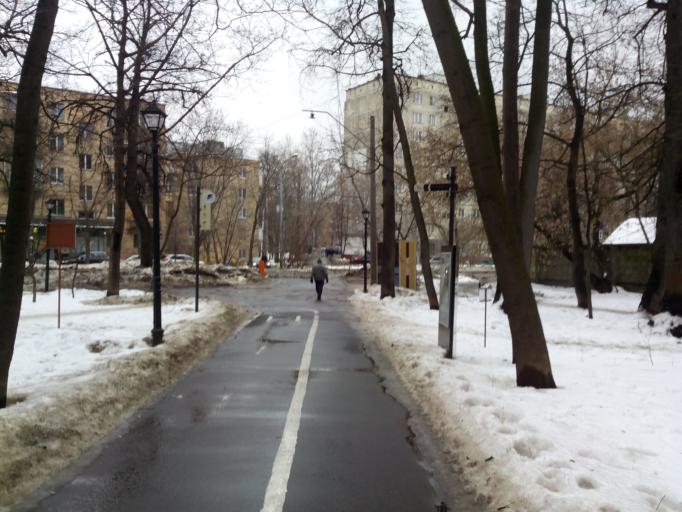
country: RU
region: Moskovskaya
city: Fili
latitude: 55.7421
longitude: 37.4751
